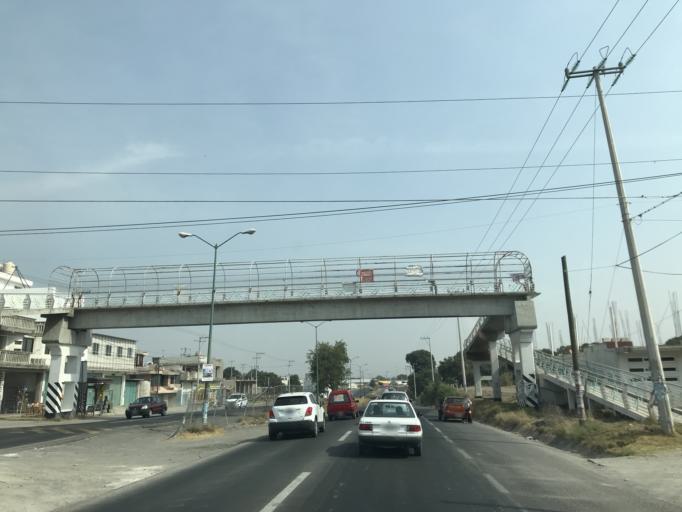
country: MX
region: Tlaxcala
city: Tenancingo
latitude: 19.1481
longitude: -98.1929
